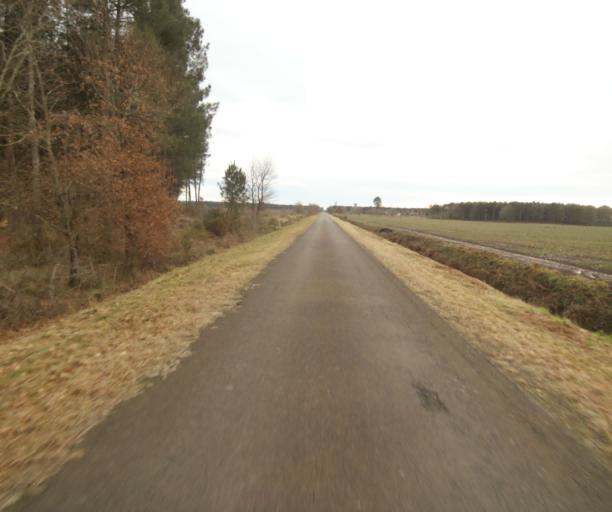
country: FR
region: Aquitaine
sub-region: Departement des Landes
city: Gabarret
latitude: 44.0317
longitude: -0.0627
